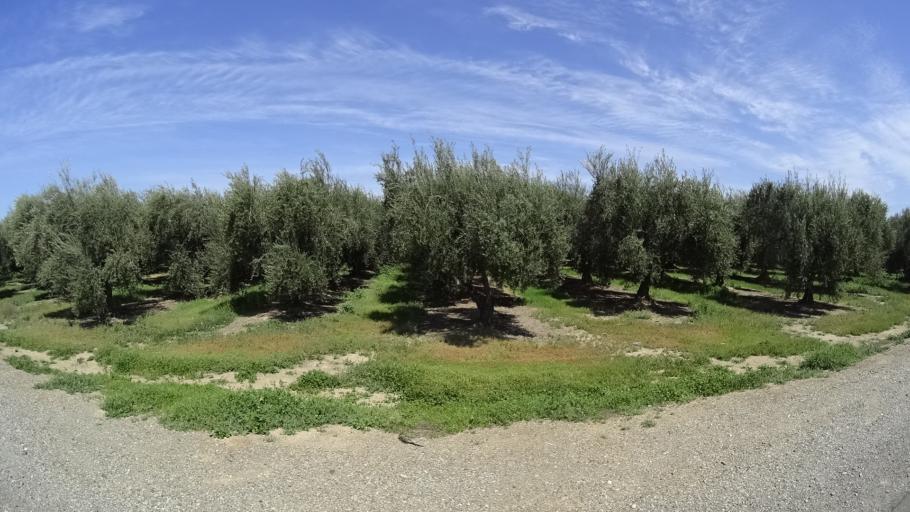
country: US
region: California
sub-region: Glenn County
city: Hamilton City
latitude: 39.6524
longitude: -122.0899
